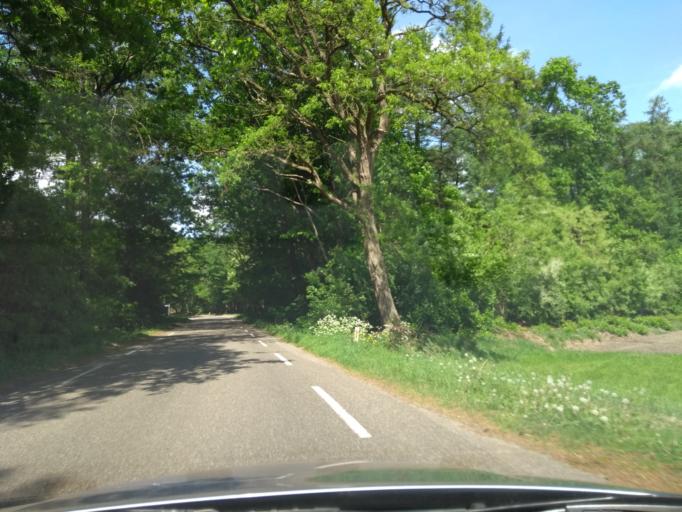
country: NL
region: Gelderland
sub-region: Gemeente Bronckhorst
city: Zelhem
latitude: 52.0515
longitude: 6.4069
